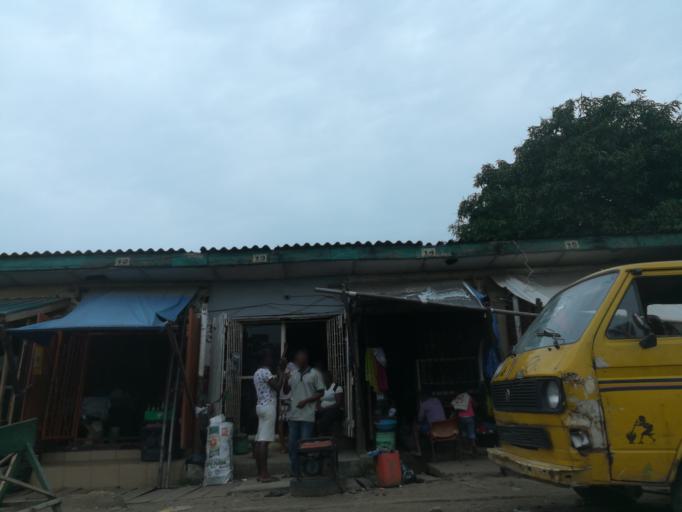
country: NG
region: Lagos
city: Makoko
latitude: 6.4953
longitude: 3.3849
